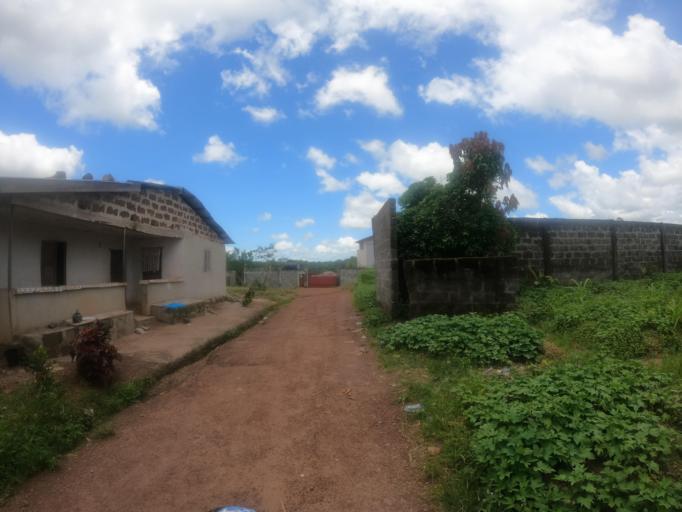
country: SL
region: Northern Province
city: Makeni
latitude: 8.8826
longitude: -12.0788
